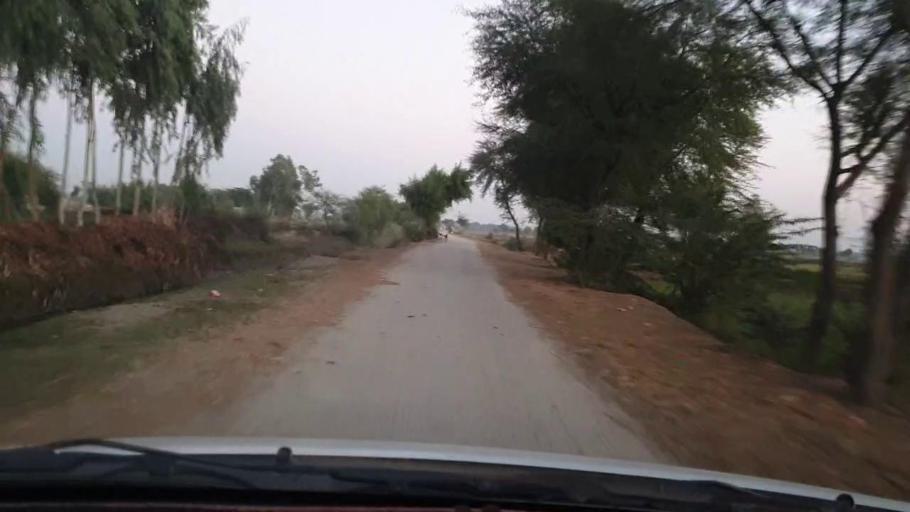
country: PK
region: Sindh
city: Khairpur Nathan Shah
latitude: 27.1448
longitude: 67.7077
